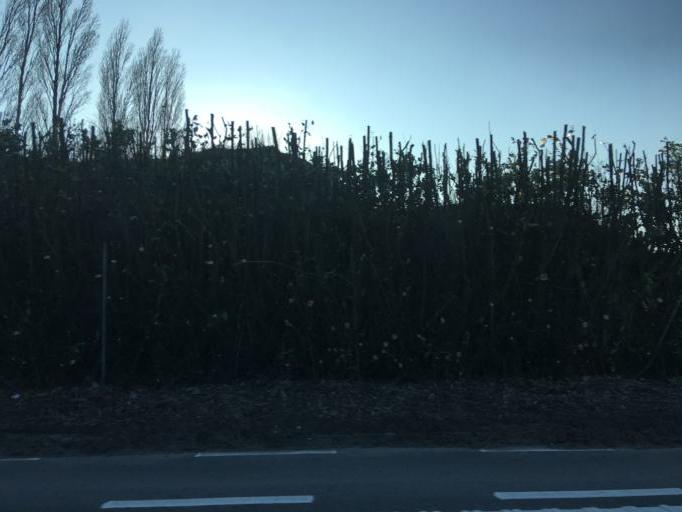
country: BE
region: Flanders
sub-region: Provincie West-Vlaanderen
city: Meulebeke
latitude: 50.9639
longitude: 3.2794
